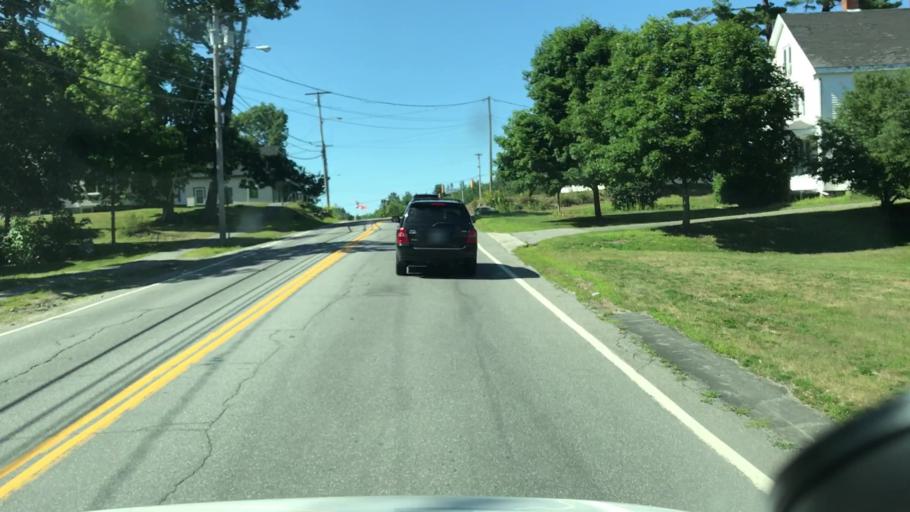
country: US
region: Maine
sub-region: Hancock County
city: Ellsworth
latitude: 44.5489
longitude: -68.4265
